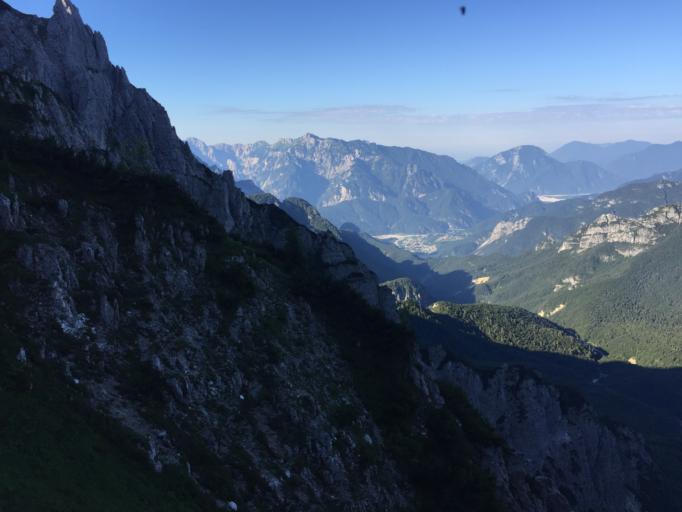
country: IT
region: Friuli Venezia Giulia
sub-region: Provincia di Udine
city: Pontebba
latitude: 46.4721
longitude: 13.2442
